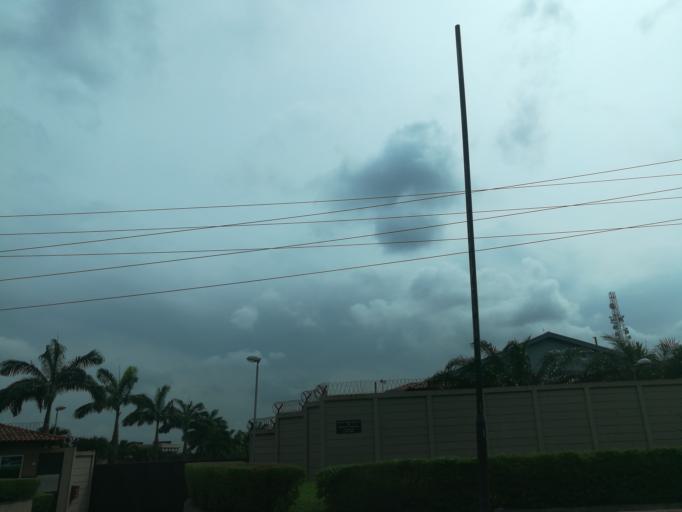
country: NG
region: Lagos
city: Ojota
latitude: 6.6080
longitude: 3.3692
